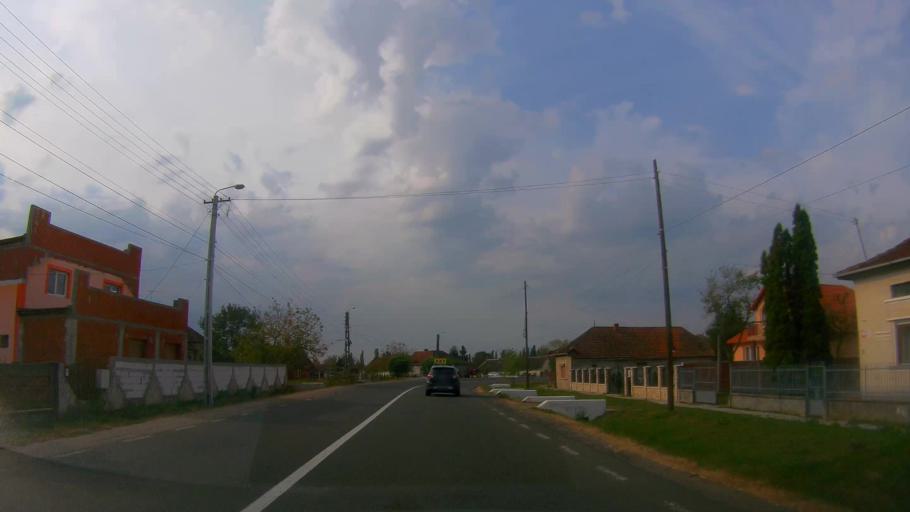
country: RO
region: Satu Mare
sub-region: Oras Ardud
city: Ardud
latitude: 47.6331
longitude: 22.8847
